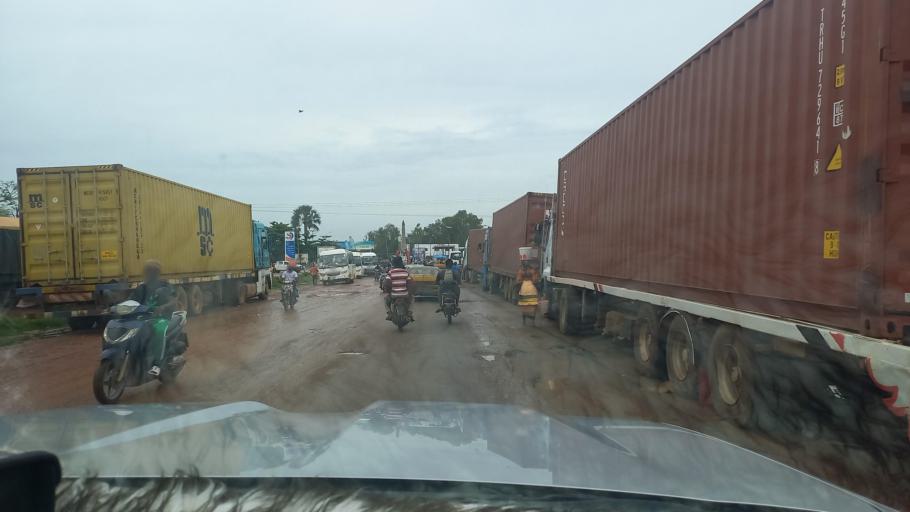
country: SN
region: Ziguinchor
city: Ziguinchor
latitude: 12.5806
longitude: -16.2645
